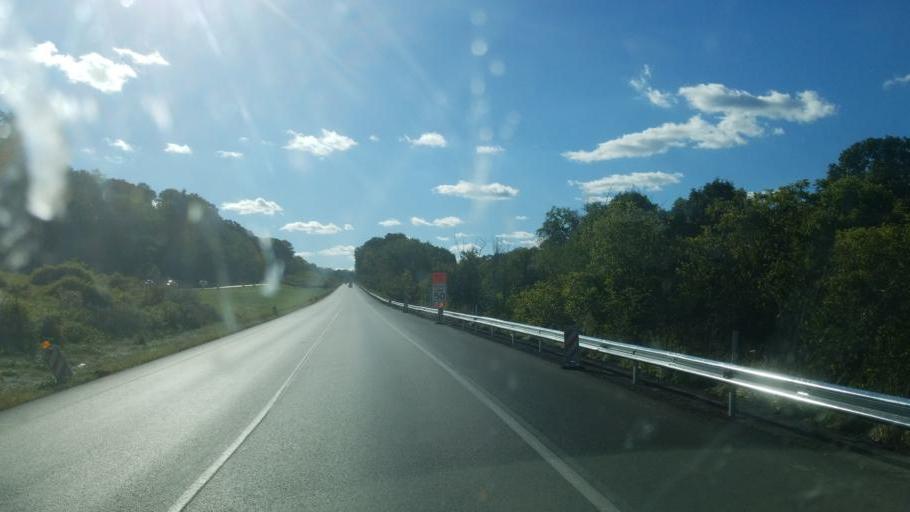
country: US
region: Pennsylvania
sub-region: Washington County
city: Wolfdale
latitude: 40.1253
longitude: -80.3767
